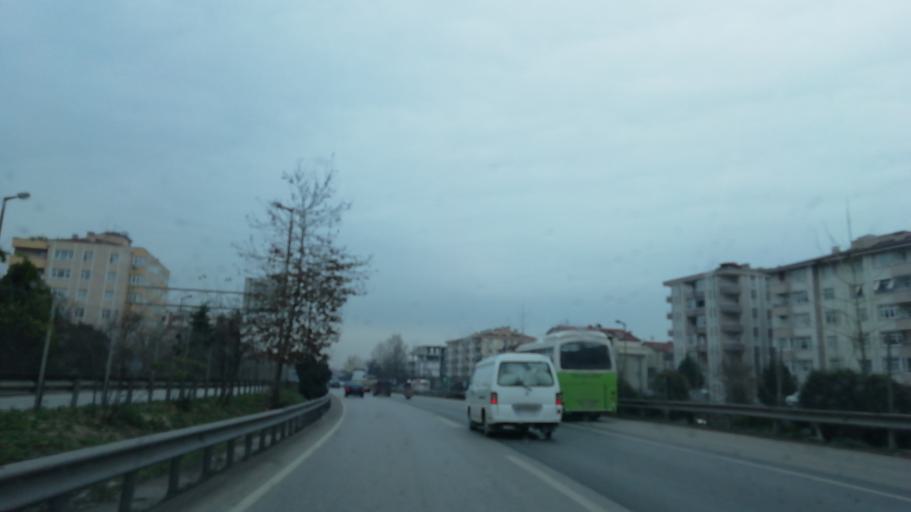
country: TR
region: Kocaeli
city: Izmit
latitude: 40.7629
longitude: 29.8786
